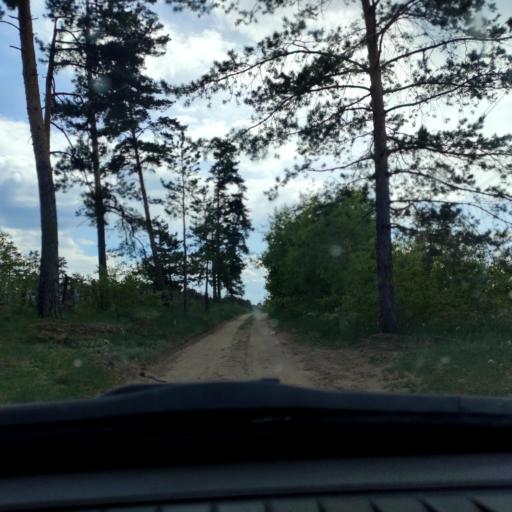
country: RU
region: Samara
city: Zhigulevsk
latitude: 53.5357
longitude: 49.5475
